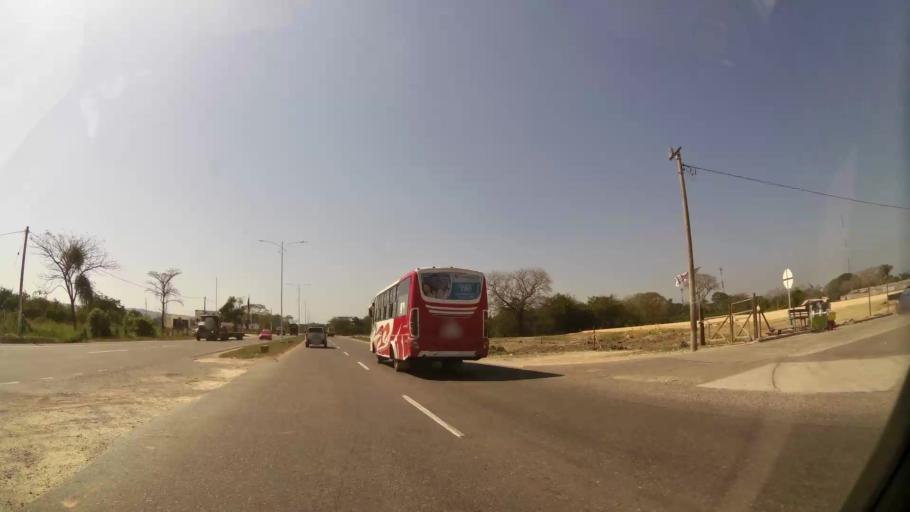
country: CO
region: Bolivar
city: Turbaco
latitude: 10.3784
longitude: -75.4512
